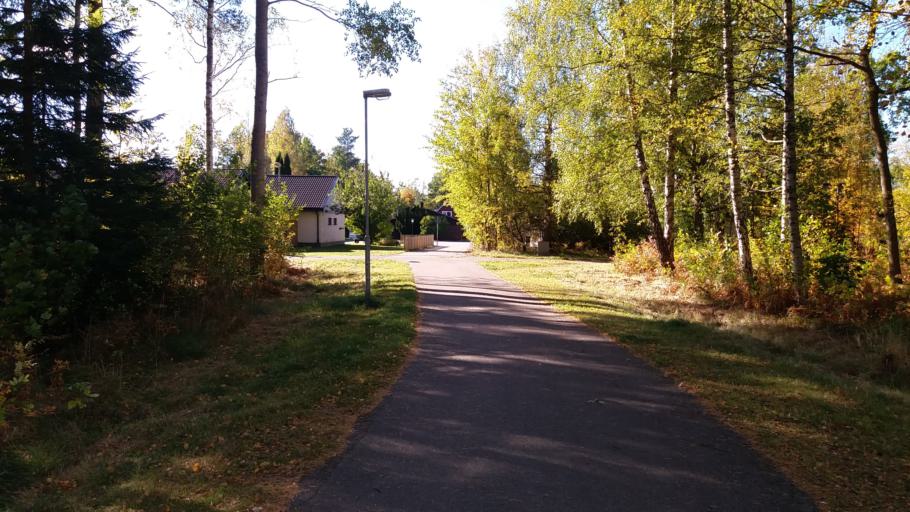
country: SE
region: OErebro
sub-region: Hallsbergs Kommun
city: Skollersta
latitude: 59.1390
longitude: 15.3341
